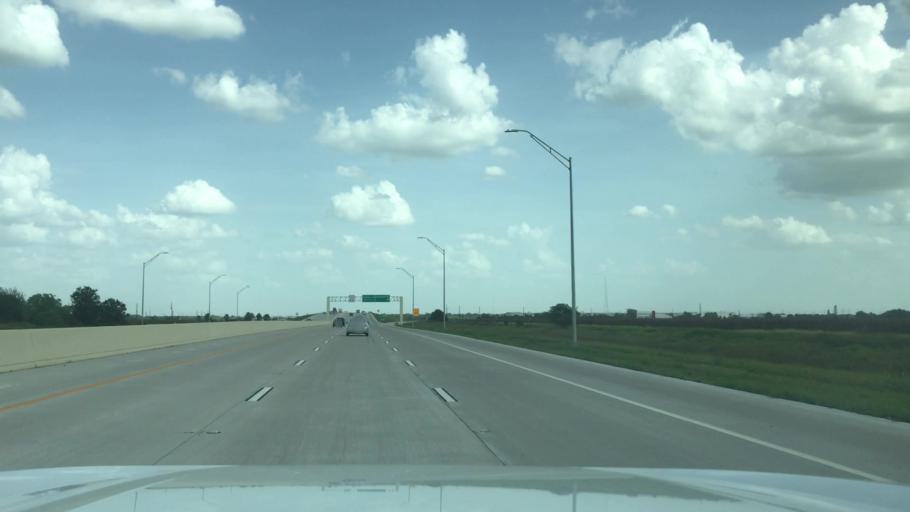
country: US
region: Texas
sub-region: Waller County
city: Waller
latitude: 30.0520
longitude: -95.8807
